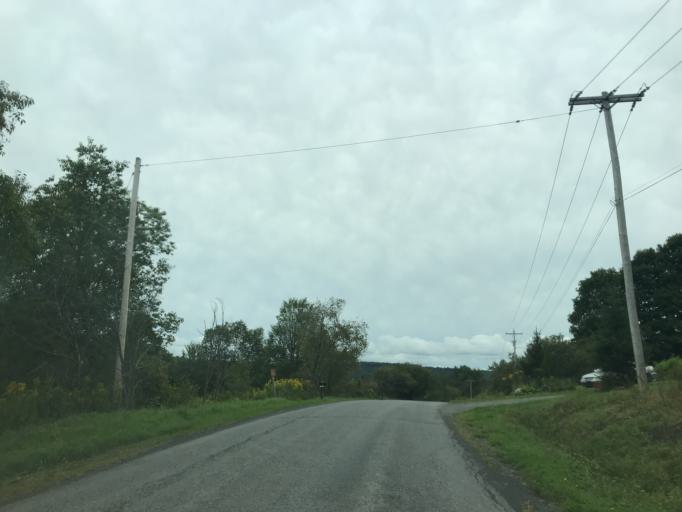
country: US
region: New York
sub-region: Otsego County
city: Worcester
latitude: 42.5612
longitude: -74.6679
